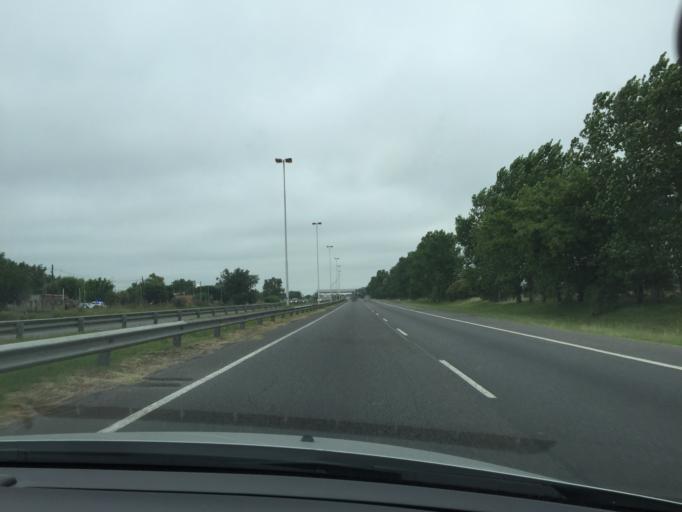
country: AR
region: Buenos Aires
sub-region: Partido de Ezeiza
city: Ezeiza
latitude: -34.8446
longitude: -58.5342
